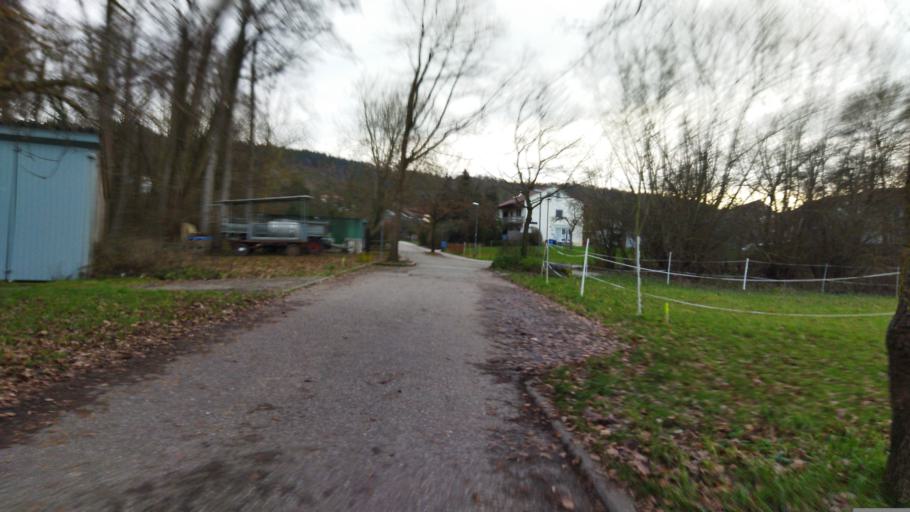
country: DE
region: Baden-Wuerttemberg
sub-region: Regierungsbezirk Stuttgart
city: Guglingen
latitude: 49.0506
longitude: 9.0025
